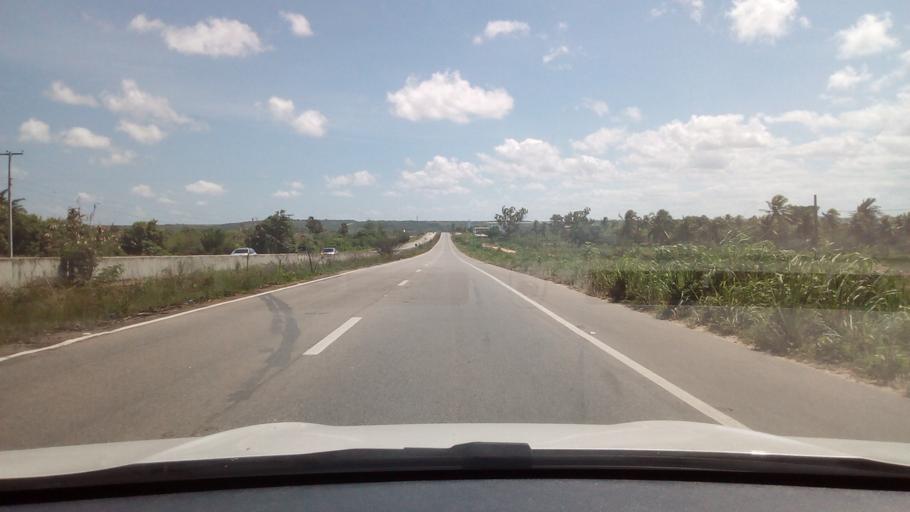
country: BR
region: Rio Grande do Norte
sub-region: Sao Jose De Mipibu
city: Sao Jose de Mipibu
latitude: -6.0823
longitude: -35.2345
